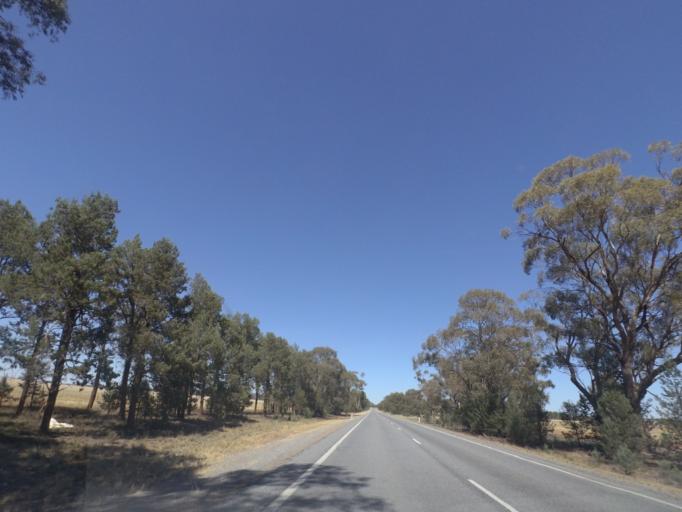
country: AU
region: New South Wales
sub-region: Narrandera
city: Narrandera
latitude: -34.4158
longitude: 146.8598
